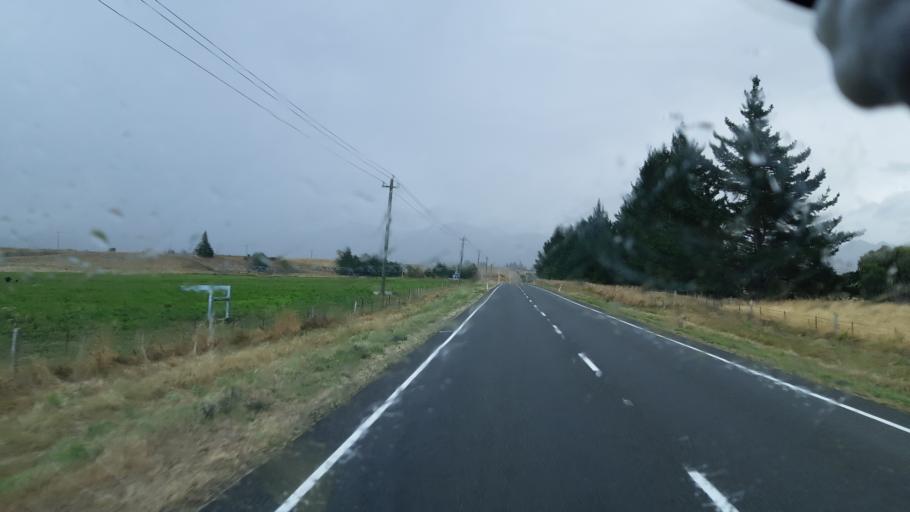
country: NZ
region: Canterbury
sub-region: Hurunui District
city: Amberley
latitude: -42.7044
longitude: 172.8224
